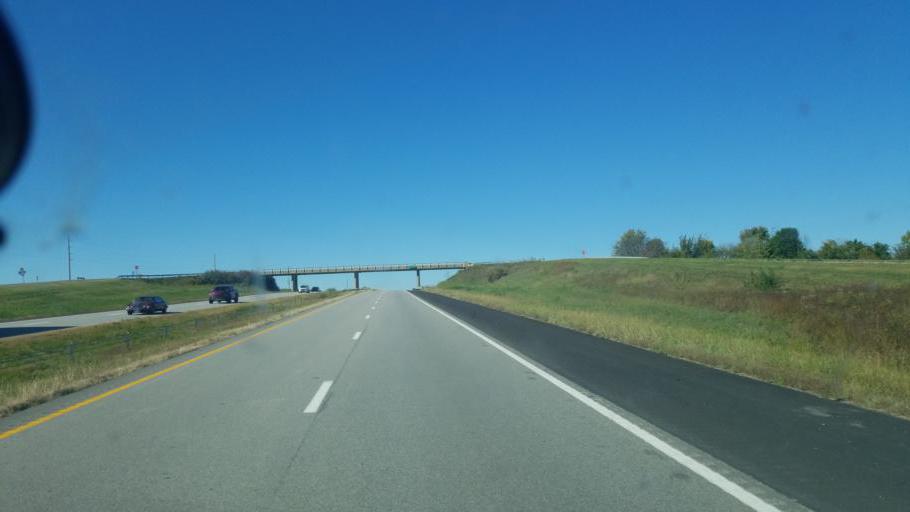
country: US
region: Missouri
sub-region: Lafayette County
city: Concordia
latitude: 38.9898
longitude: -93.6302
